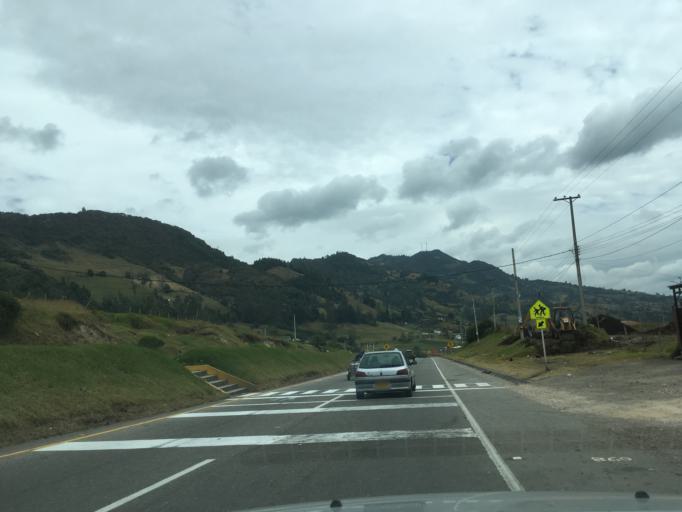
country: CO
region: Boyaca
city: Ventaquemada
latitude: 5.3658
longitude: -73.5305
